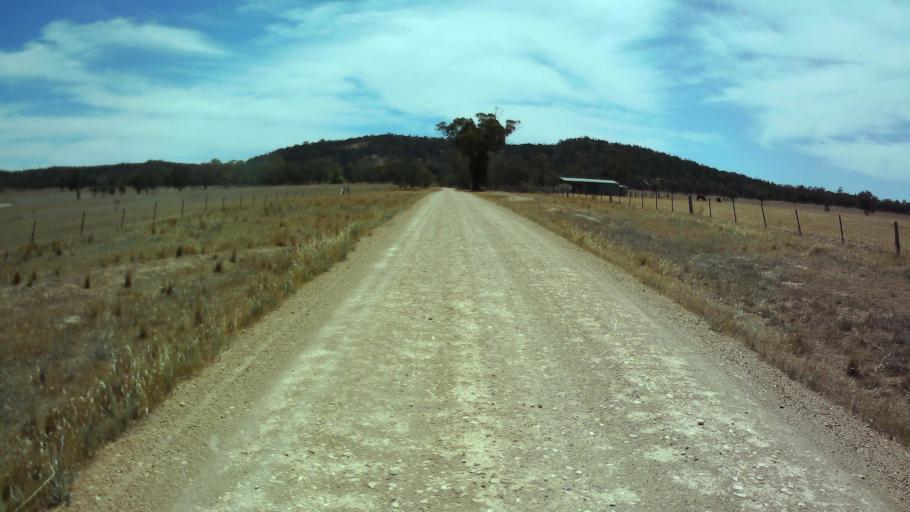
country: AU
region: New South Wales
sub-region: Weddin
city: Grenfell
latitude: -33.7484
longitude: 148.2028
